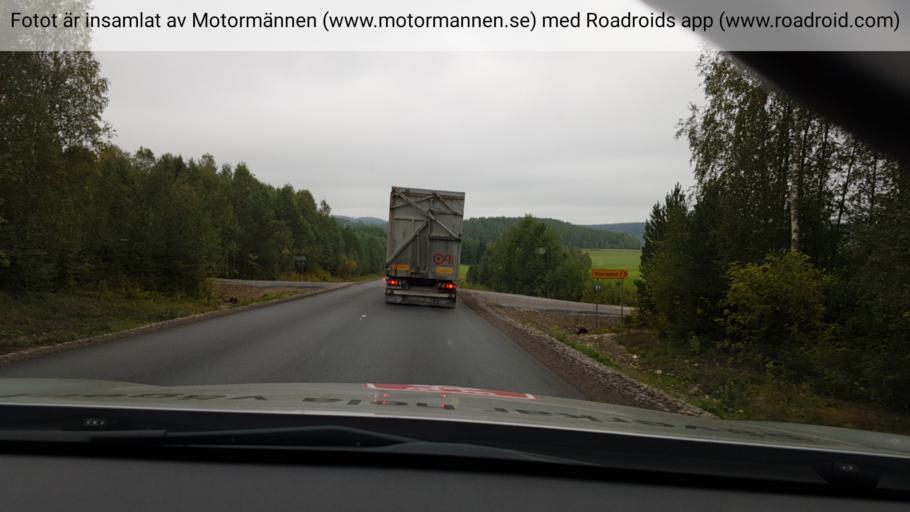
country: SE
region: Vaesterbotten
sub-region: Skelleftea Kommun
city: Burtraesk
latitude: 64.3716
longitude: 20.5040
